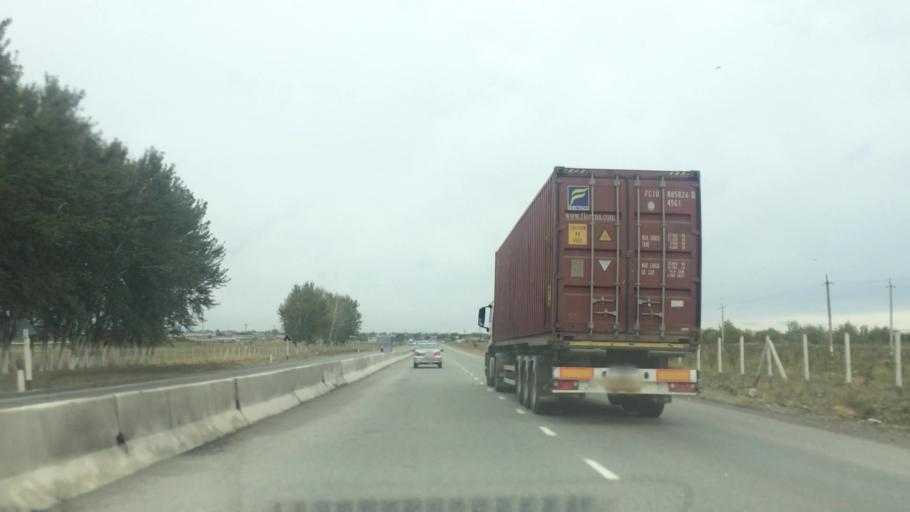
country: UZ
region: Samarqand
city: Bulung'ur
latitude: 39.7790
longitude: 67.2931
